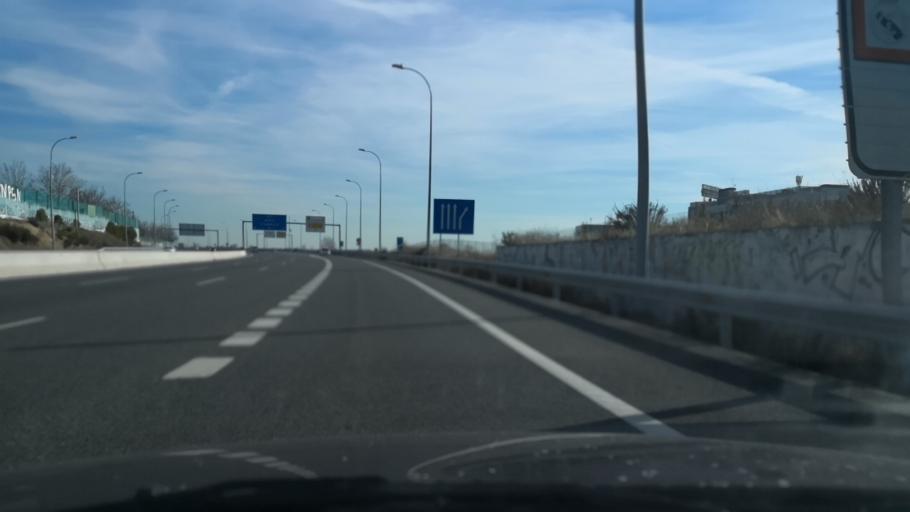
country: ES
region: Madrid
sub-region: Provincia de Madrid
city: Hortaleza
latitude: 40.4757
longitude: -3.6312
